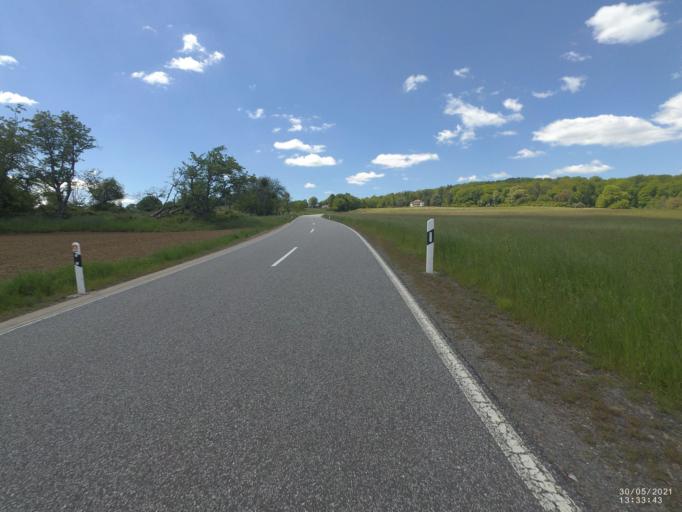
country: DE
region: Rheinland-Pfalz
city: Rhens
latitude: 50.2831
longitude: 7.5923
